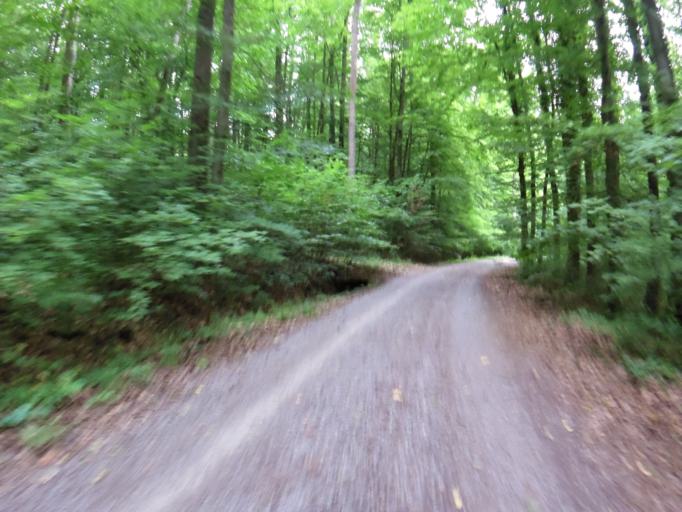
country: DE
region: Bavaria
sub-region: Regierungsbezirk Unterfranken
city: Margetshochheim
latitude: 49.8219
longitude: 9.8431
